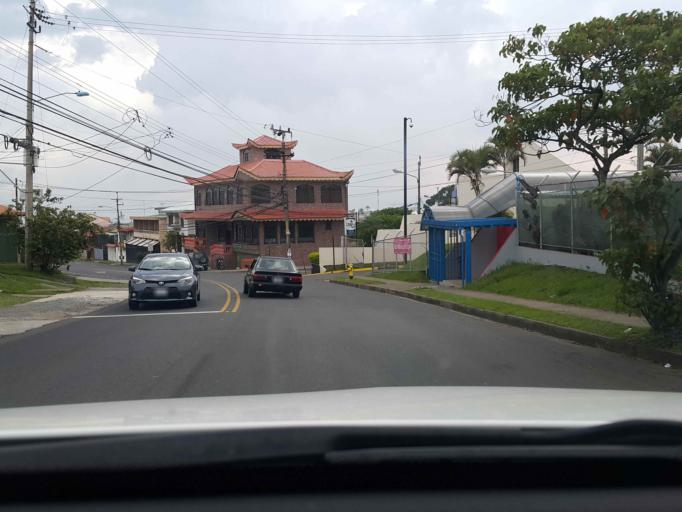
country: CR
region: Heredia
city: San Pablo
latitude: 9.9991
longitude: -84.1056
